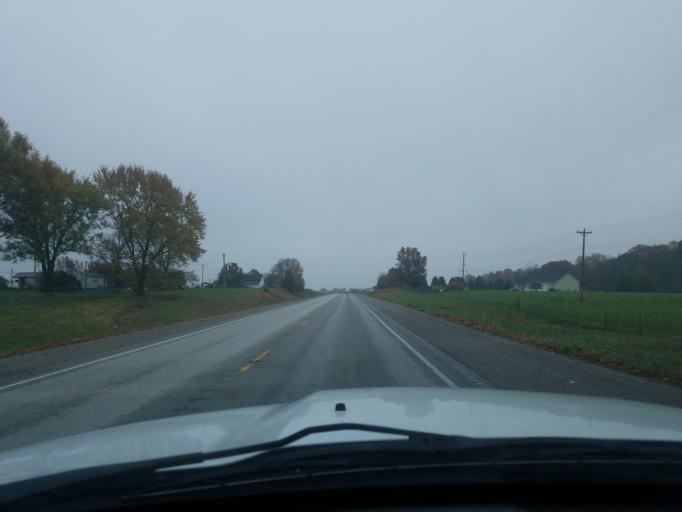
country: US
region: Kentucky
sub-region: Taylor County
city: Campbellsville
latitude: 37.3618
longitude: -85.3148
